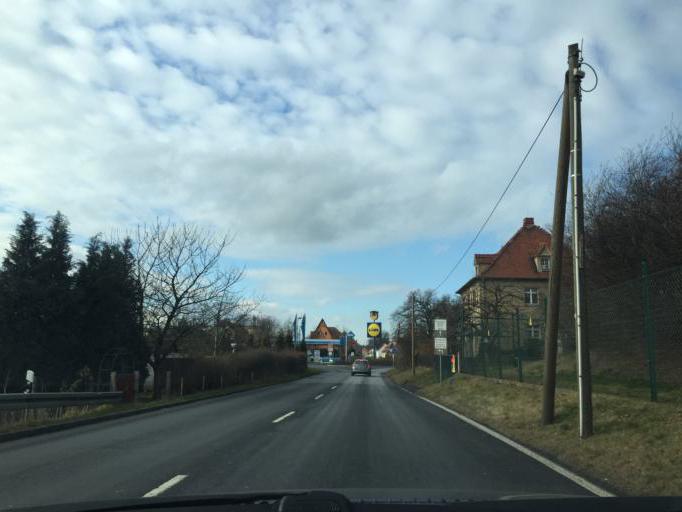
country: DE
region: Saxony
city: Radeburg
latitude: 51.2139
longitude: 13.7328
